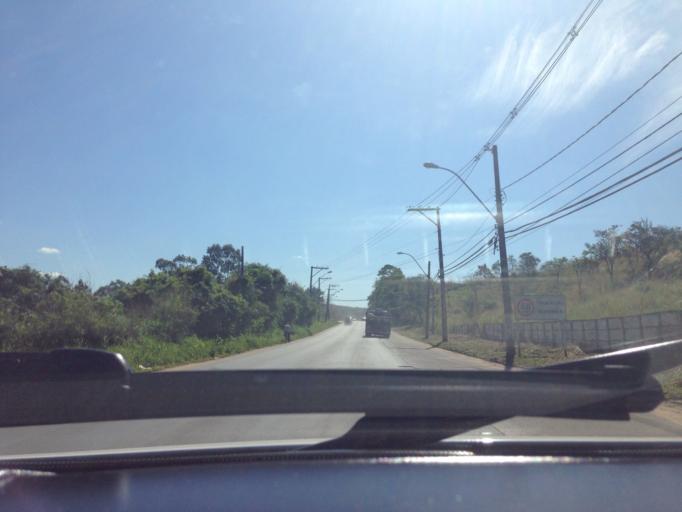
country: BR
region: Espirito Santo
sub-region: Guarapari
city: Guarapari
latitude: -20.6338
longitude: -40.4791
